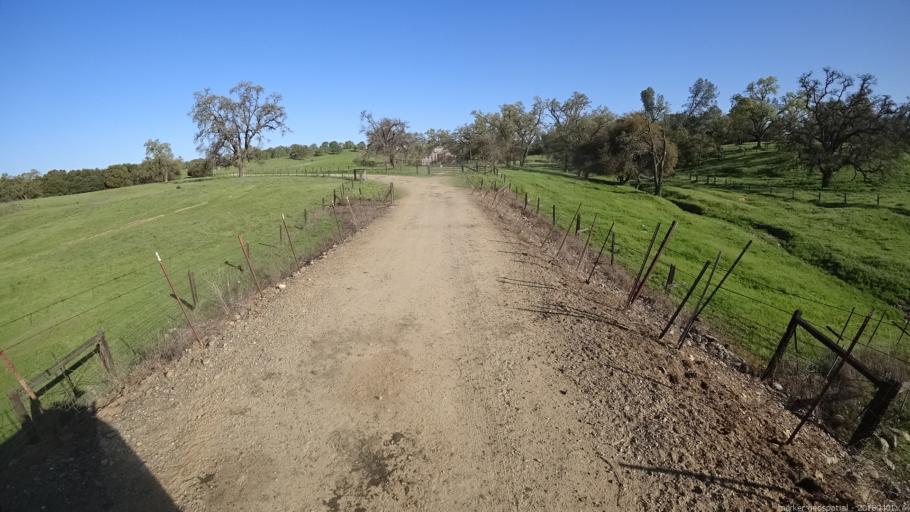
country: US
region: California
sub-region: Sacramento County
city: Rancho Murieta
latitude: 38.5011
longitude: -121.0456
